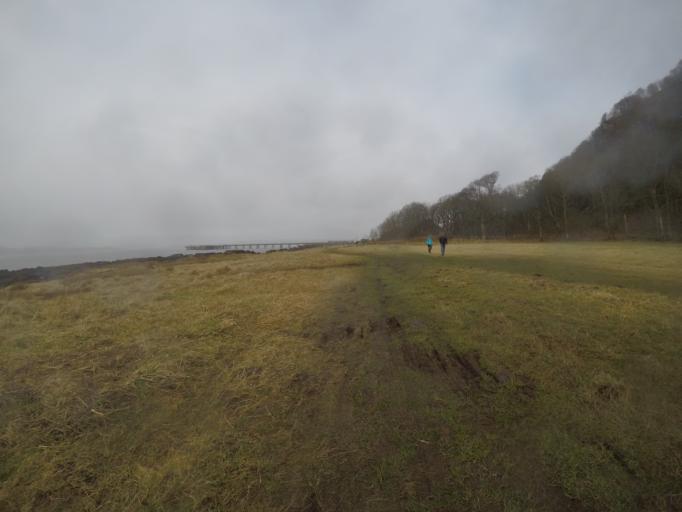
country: GB
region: Scotland
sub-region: North Ayrshire
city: Millport
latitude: 55.7123
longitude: -4.9033
